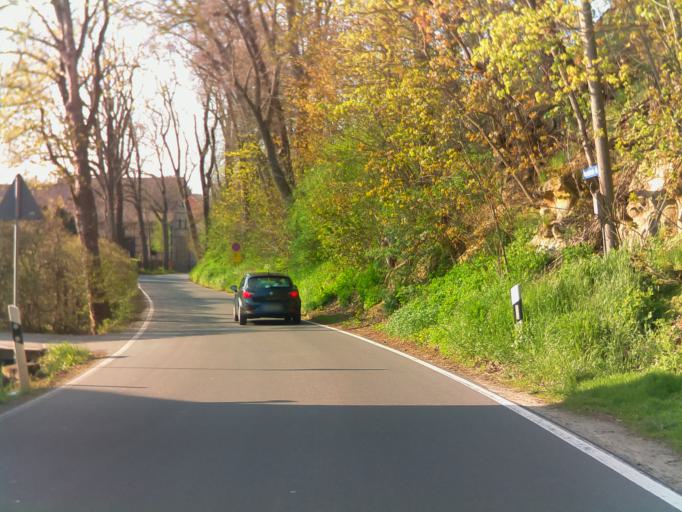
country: DE
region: Thuringia
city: Herschdorf
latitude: 50.7222
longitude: 11.5399
